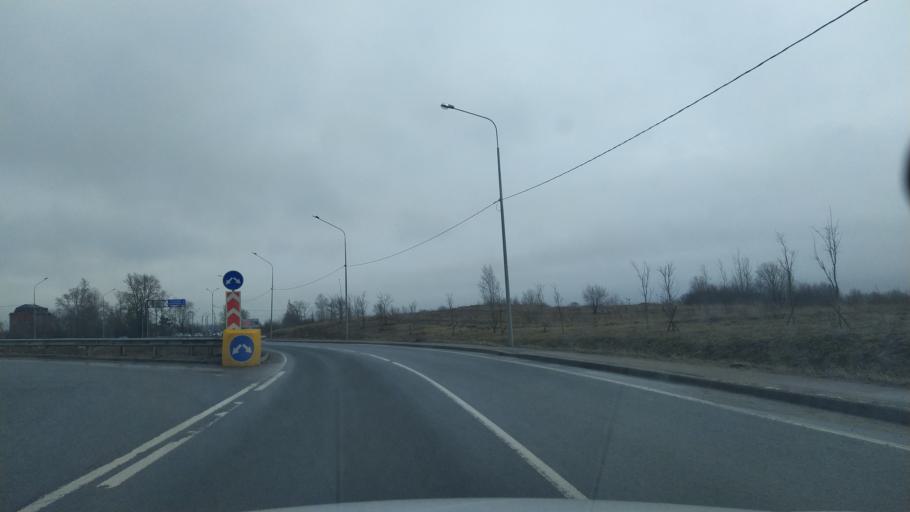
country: RU
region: St.-Petersburg
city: Aleksandrovskaya
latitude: 59.7158
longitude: 30.2922
